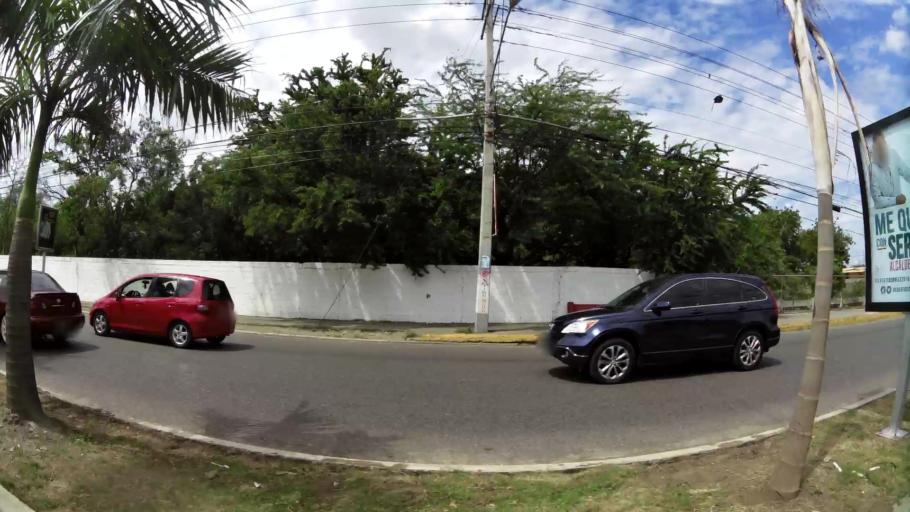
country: DO
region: Santiago
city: Santiago de los Caballeros
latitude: 19.4700
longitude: -70.7131
